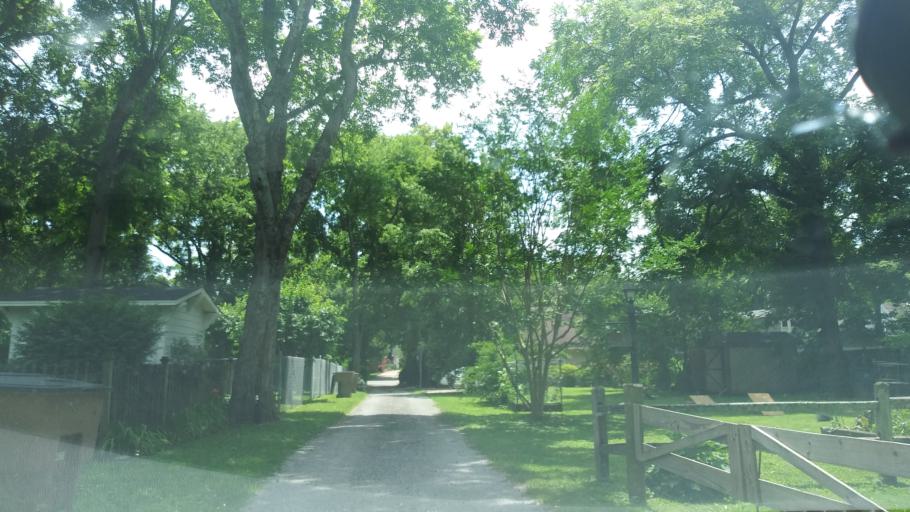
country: US
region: Tennessee
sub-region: Davidson County
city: Belle Meade
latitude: 36.1379
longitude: -86.8343
